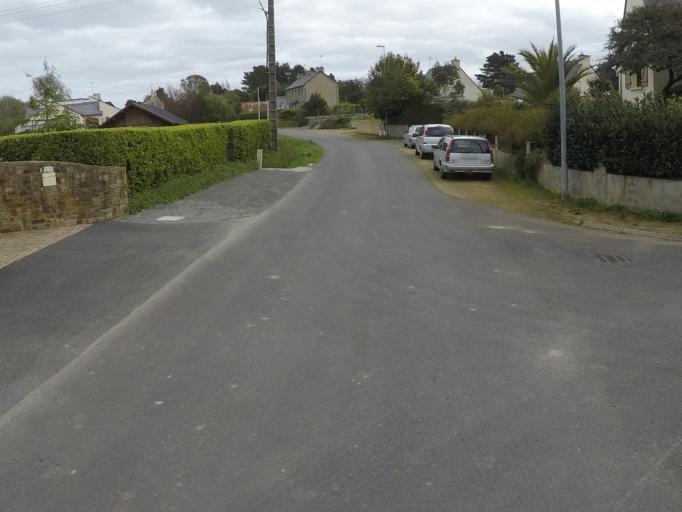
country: FR
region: Brittany
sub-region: Departement des Cotes-d'Armor
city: Plouha
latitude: 48.6819
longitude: -2.9265
